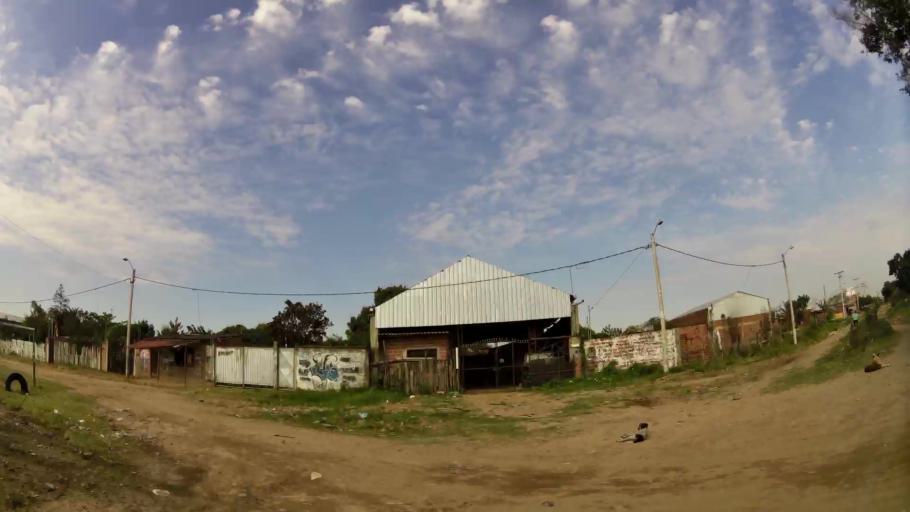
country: BO
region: Santa Cruz
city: Santa Cruz de la Sierra
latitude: -17.7368
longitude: -63.1386
